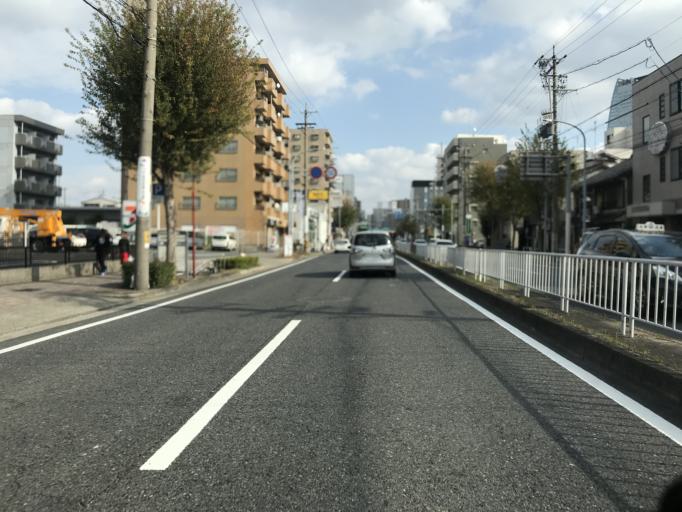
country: JP
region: Aichi
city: Nagoya-shi
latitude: 35.1762
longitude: 136.8757
